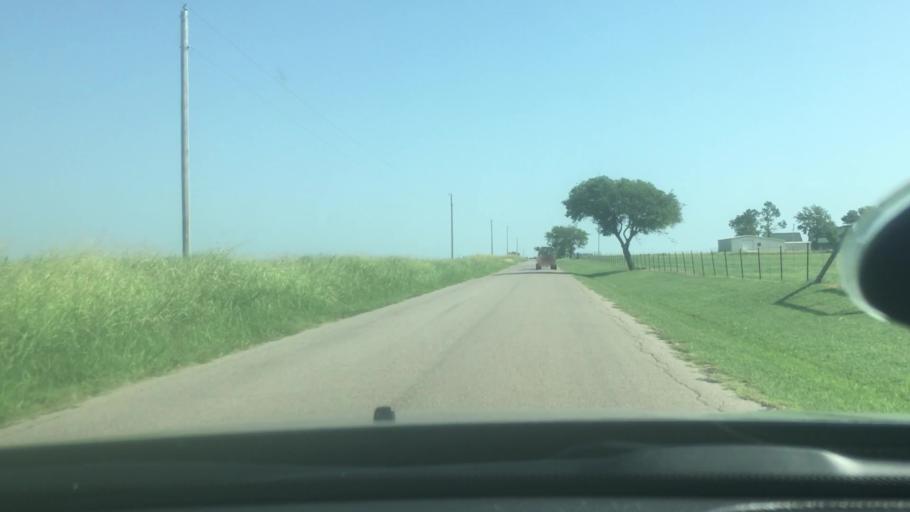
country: US
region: Oklahoma
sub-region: Bryan County
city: Calera
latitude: 33.9744
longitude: -96.4656
